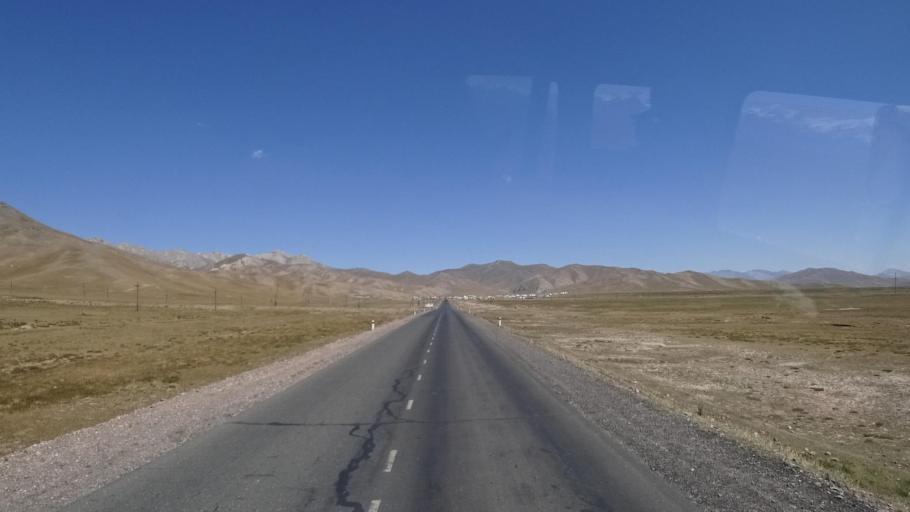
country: KG
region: Osh
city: Gul'cha
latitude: 39.7111
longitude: 73.2351
